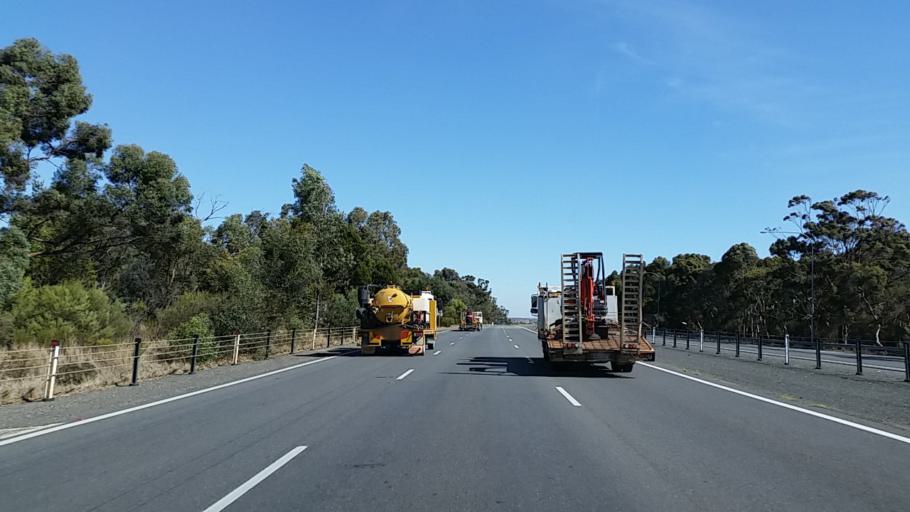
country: AU
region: South Australia
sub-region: Light
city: Willaston
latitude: -34.5735
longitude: 138.7444
